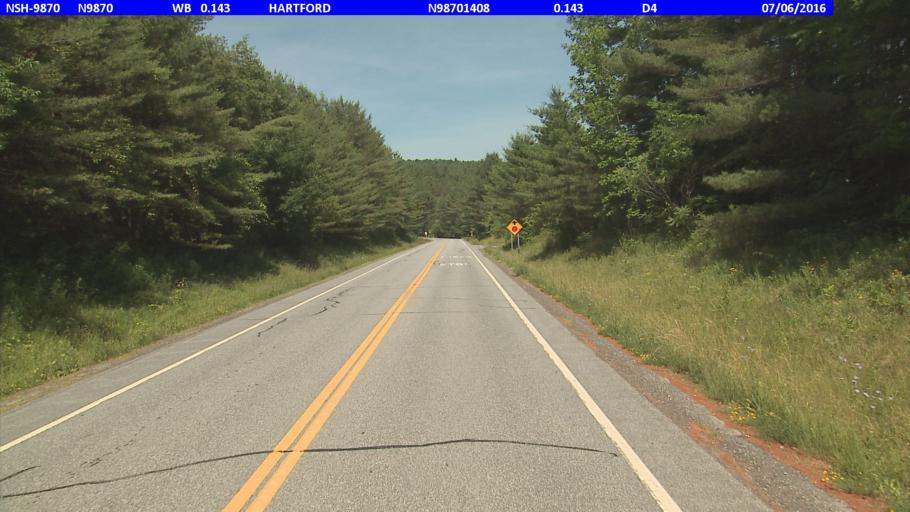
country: US
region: Vermont
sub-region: Windsor County
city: Wilder
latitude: 43.6680
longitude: -72.3232
